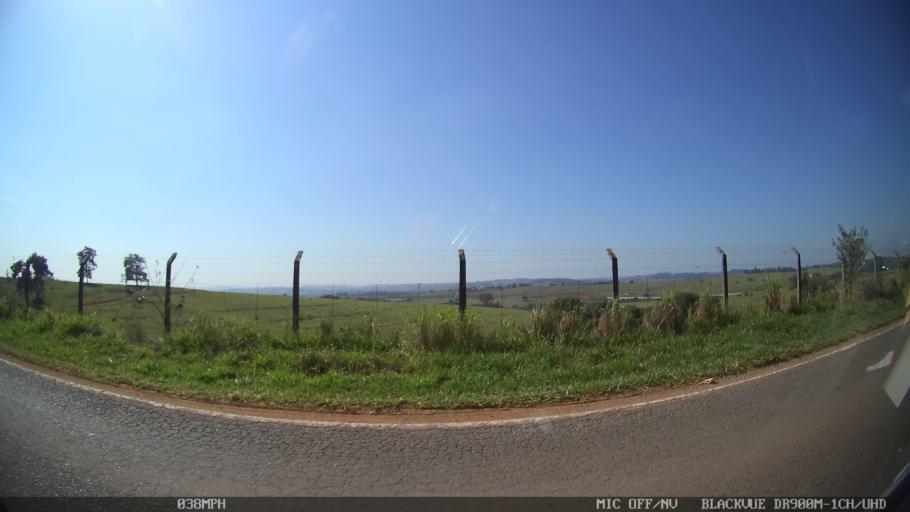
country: BR
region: Sao Paulo
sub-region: Valinhos
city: Valinhos
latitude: -23.0277
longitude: -47.0985
